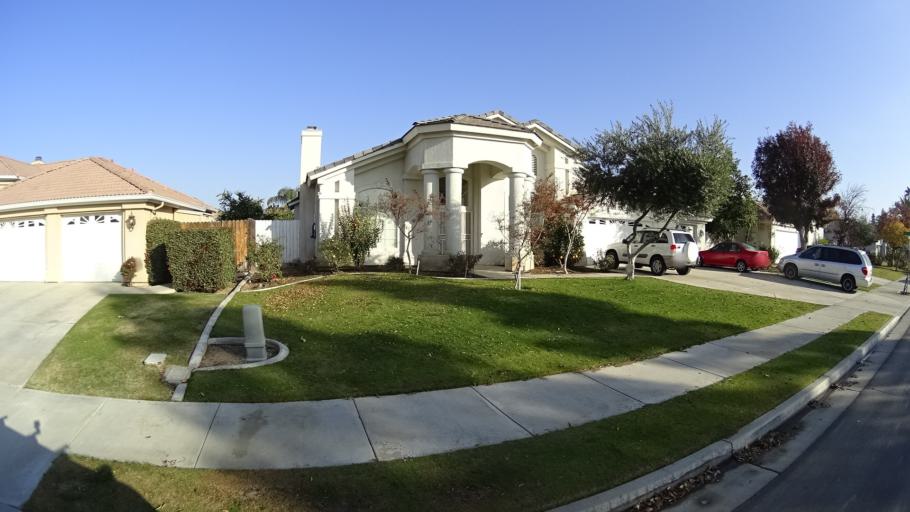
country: US
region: California
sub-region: Kern County
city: Greenacres
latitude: 35.3675
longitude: -119.1241
